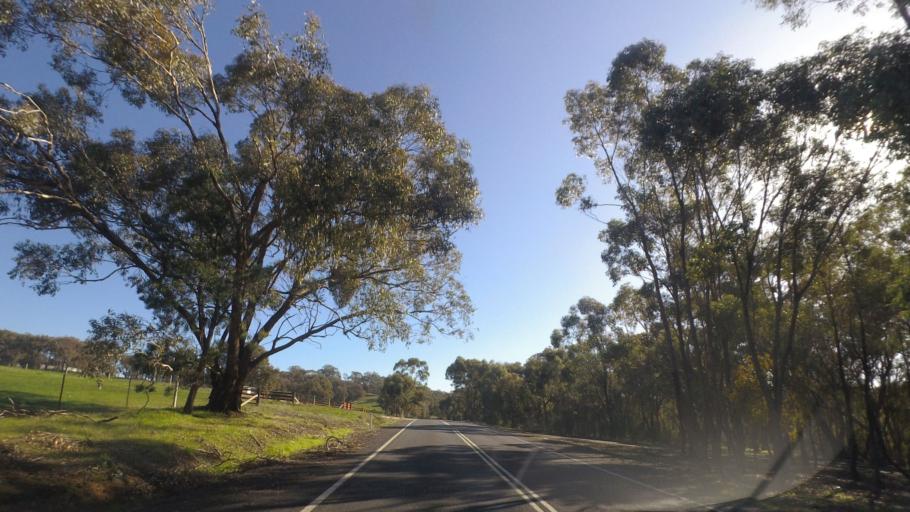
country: AU
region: Victoria
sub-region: Greater Bendigo
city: Kennington
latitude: -36.9192
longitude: 144.3389
